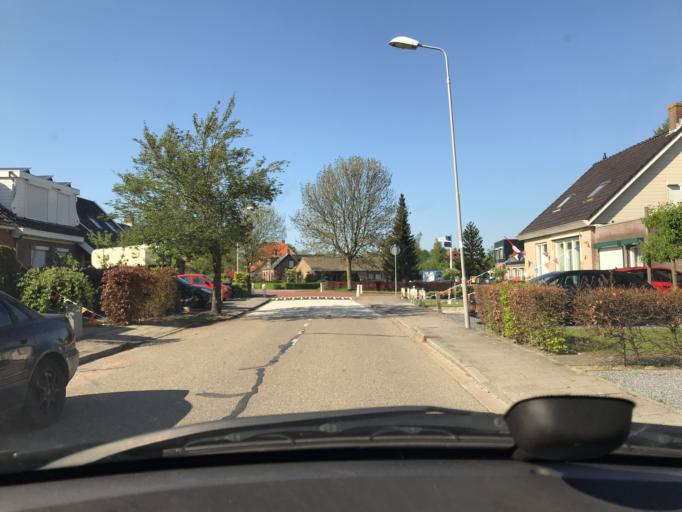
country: NL
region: Zeeland
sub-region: Gemeente Goes
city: Goes
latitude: 51.5327
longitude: 3.8157
